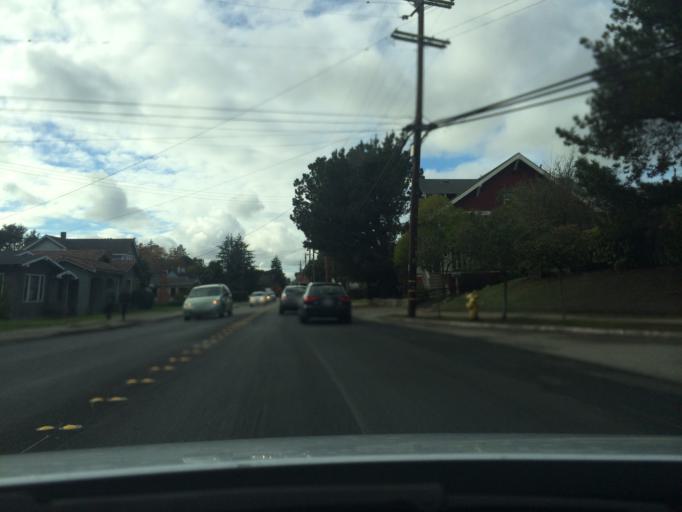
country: US
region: California
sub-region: Sonoma County
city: Petaluma
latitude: 38.2343
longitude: -122.6476
